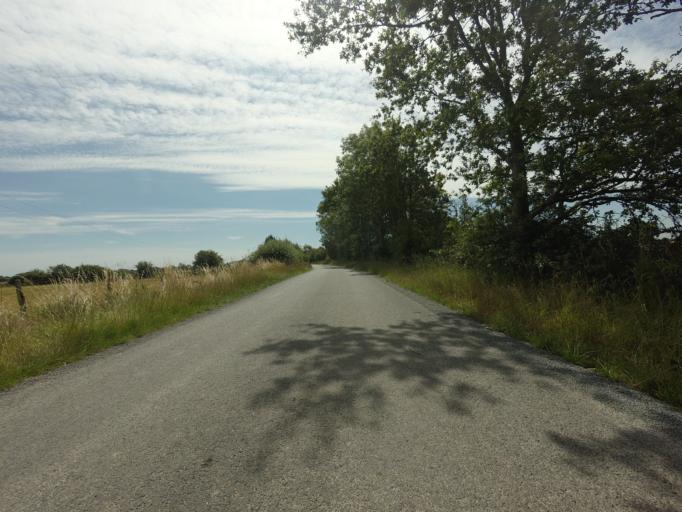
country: GB
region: England
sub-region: Kent
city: Stone
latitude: 51.0070
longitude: 0.7949
